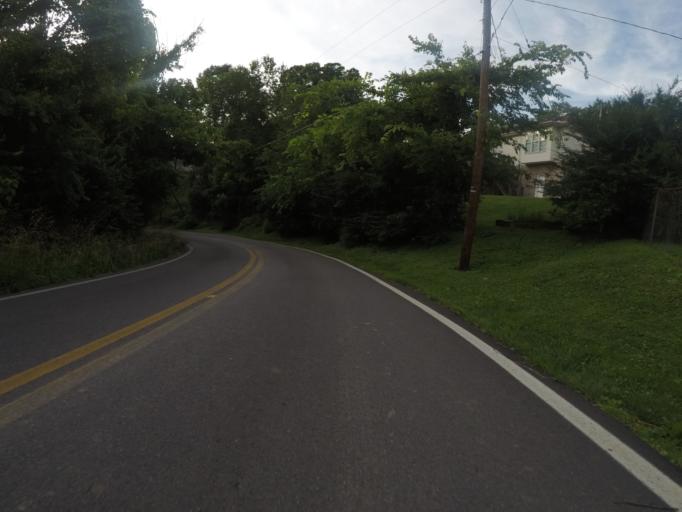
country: US
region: West Virginia
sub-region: Cabell County
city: Pea Ridge
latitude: 38.4053
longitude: -82.3620
